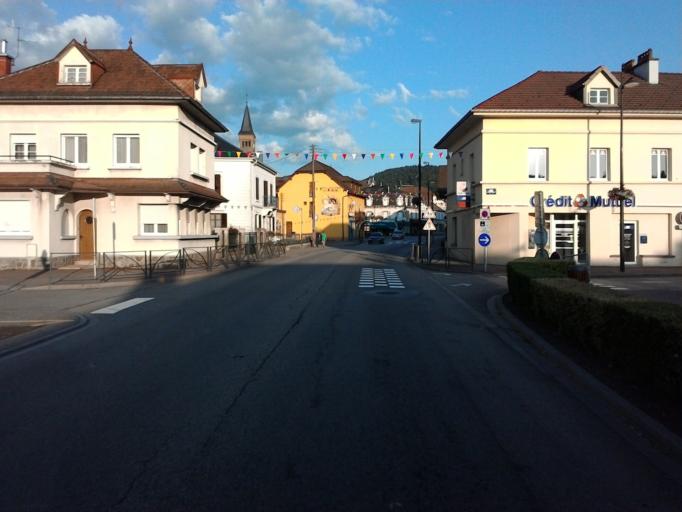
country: FR
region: Lorraine
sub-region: Departement des Vosges
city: Le Thillot
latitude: 47.8807
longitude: 6.7634
